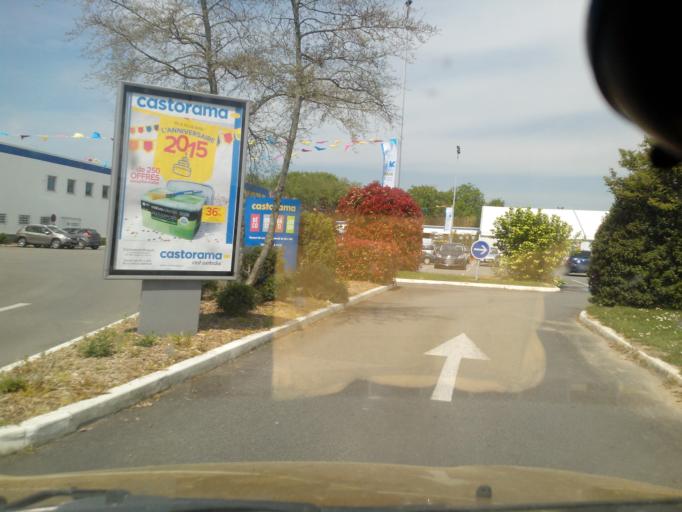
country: FR
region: Pays de la Loire
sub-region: Departement de la Loire-Atlantique
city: Orvault
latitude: 47.2537
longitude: -1.6198
